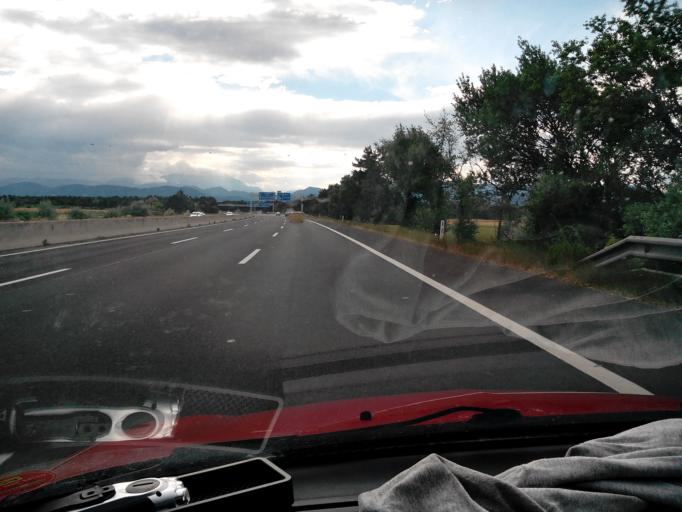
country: AT
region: Lower Austria
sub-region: Wiener Neustadt Stadt
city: Wiener Neustadt
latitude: 47.7884
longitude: 16.2188
